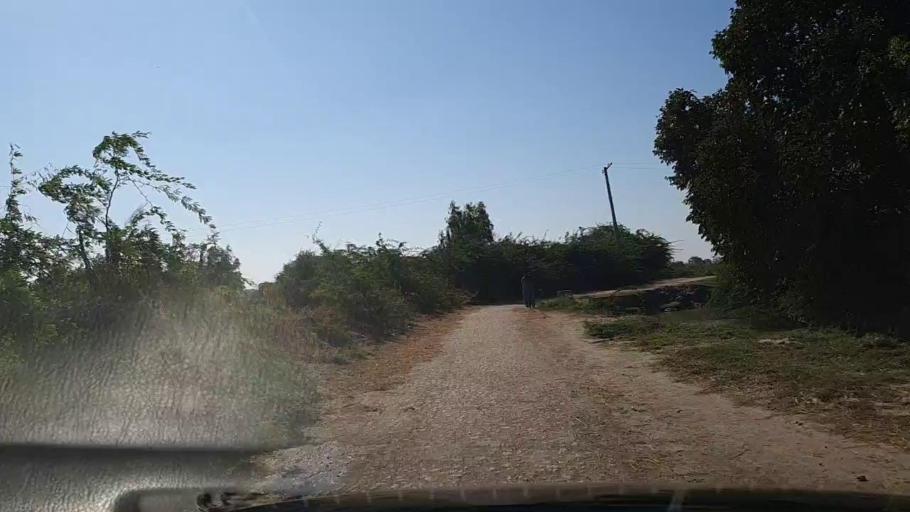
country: PK
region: Sindh
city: Thatta
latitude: 24.7097
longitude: 67.9189
